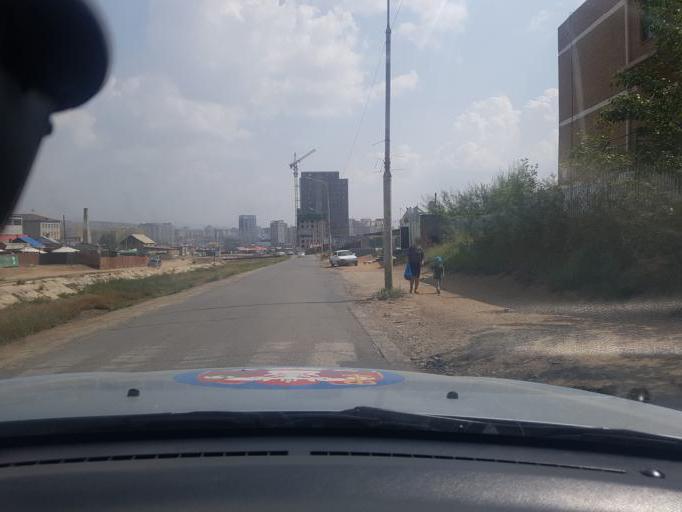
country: MN
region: Ulaanbaatar
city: Ulaanbaatar
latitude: 47.9361
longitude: 106.9023
